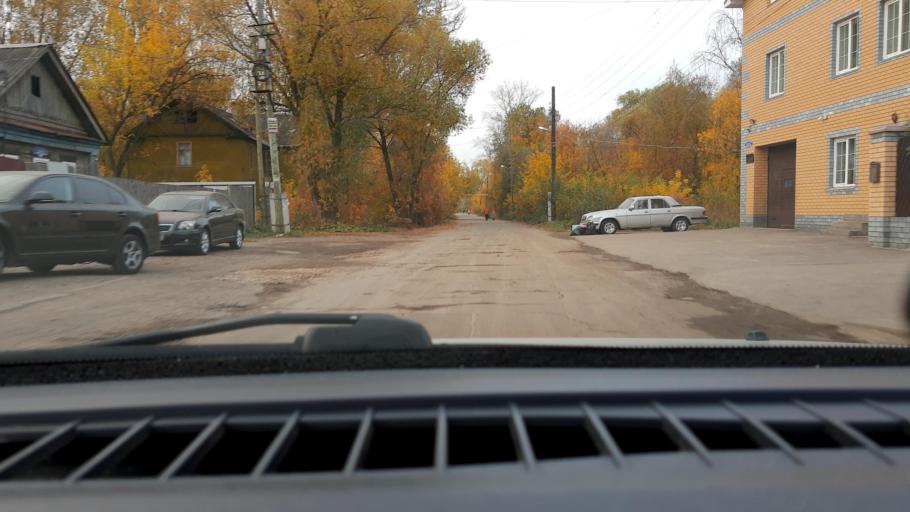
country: RU
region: Nizjnij Novgorod
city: Gorbatovka
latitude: 56.3470
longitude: 43.8342
